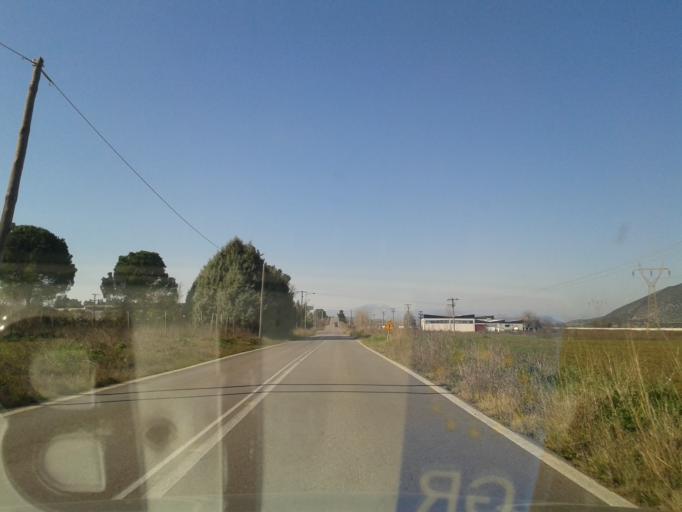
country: GR
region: Central Greece
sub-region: Nomos Voiotias
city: Arma
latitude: 38.3773
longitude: 23.4717
